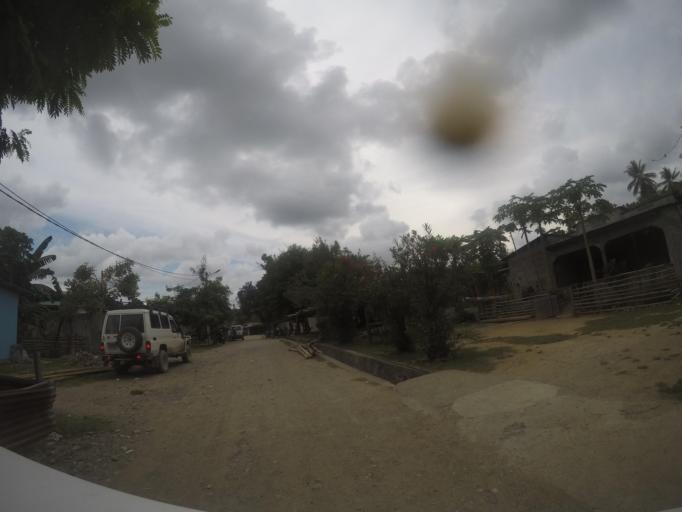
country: TL
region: Viqueque
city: Viqueque
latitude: -8.8777
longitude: 126.3634
